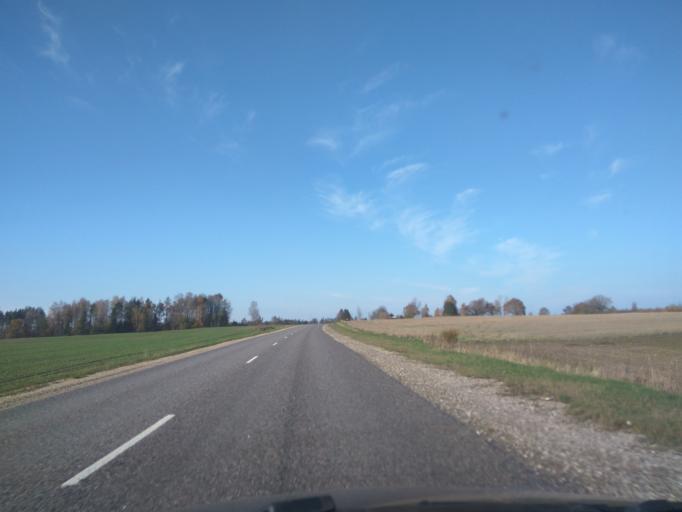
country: LV
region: Kuldigas Rajons
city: Kuldiga
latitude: 57.0325
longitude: 21.8433
